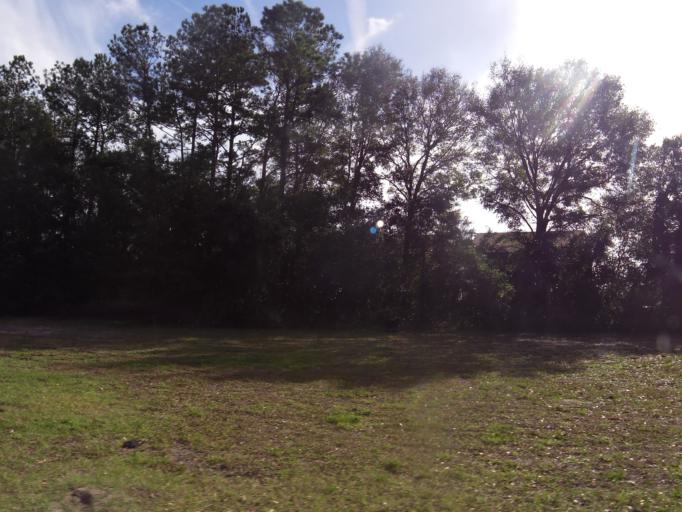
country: US
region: Florida
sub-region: Duval County
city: Jacksonville
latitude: 30.3308
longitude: -81.5436
